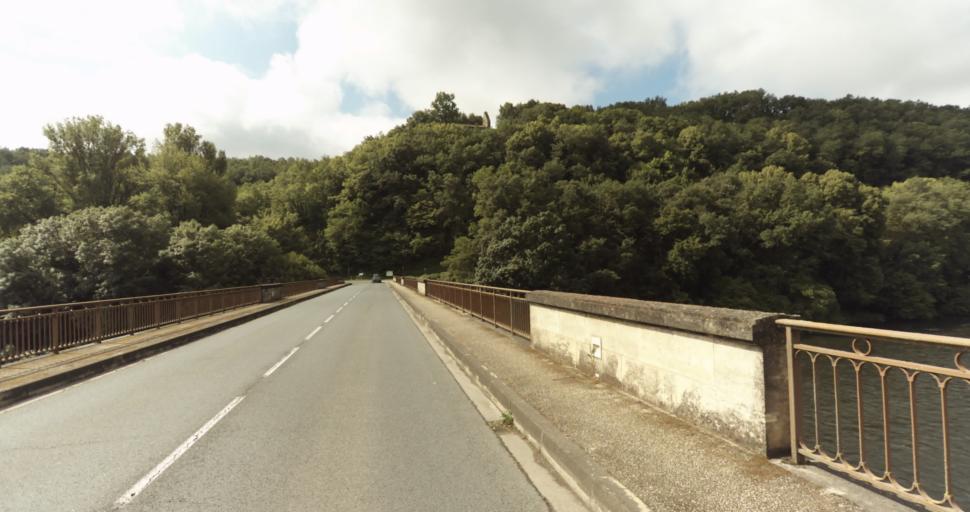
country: FR
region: Aquitaine
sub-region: Departement de la Dordogne
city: Lalinde
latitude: 44.8345
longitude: 0.7403
